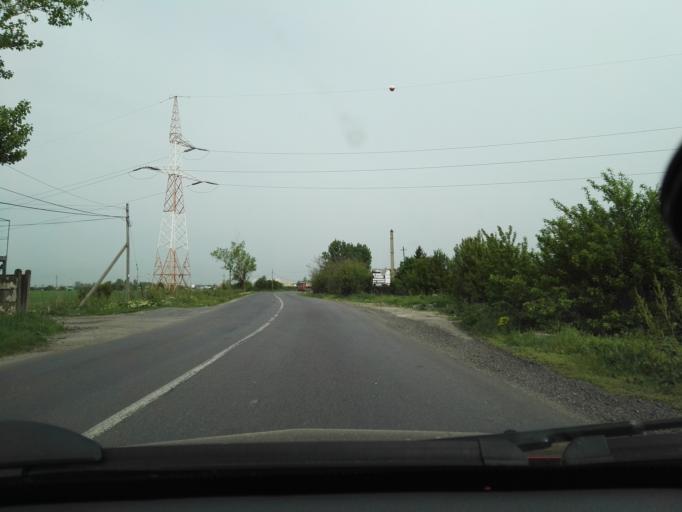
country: RO
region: Ilfov
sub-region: Comuna Magurele
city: Magurele
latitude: 44.3657
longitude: 26.0195
